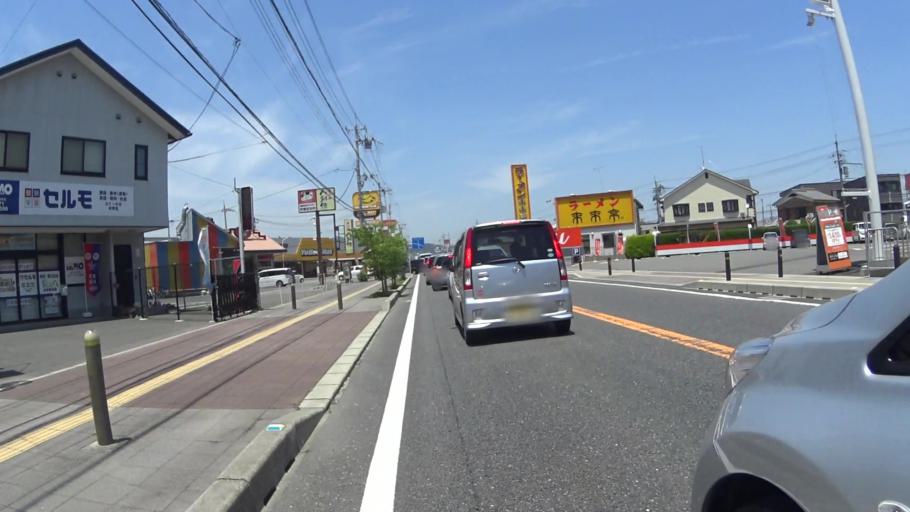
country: JP
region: Kyoto
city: Fukuchiyama
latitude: 35.2751
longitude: 135.1832
